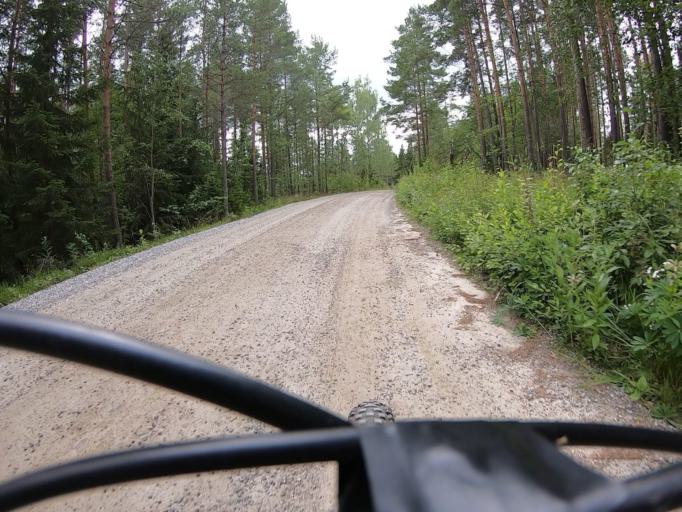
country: FI
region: Varsinais-Suomi
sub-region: Vakka-Suomi
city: Uusikaupunki
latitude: 60.8447
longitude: 21.3895
